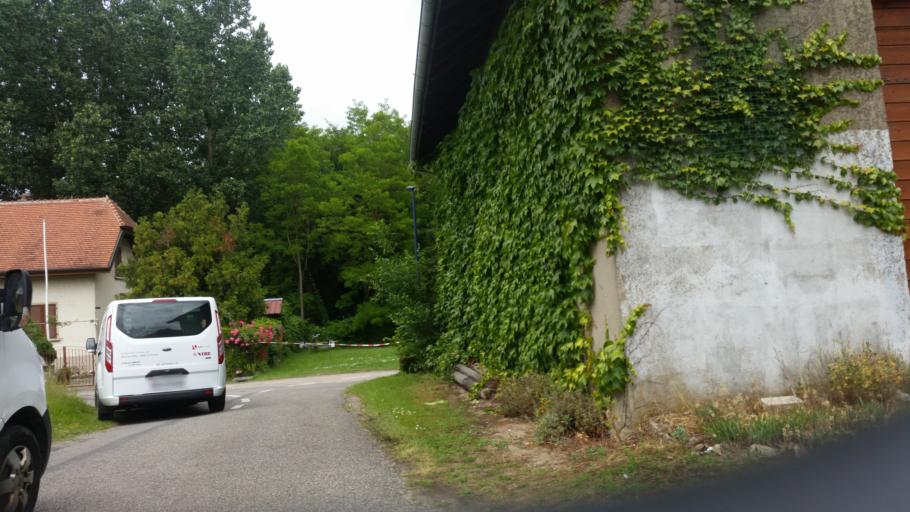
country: CH
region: Vaud
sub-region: Jura-Nord vaudois District
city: Yvonand
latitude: 46.8030
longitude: 6.7398
